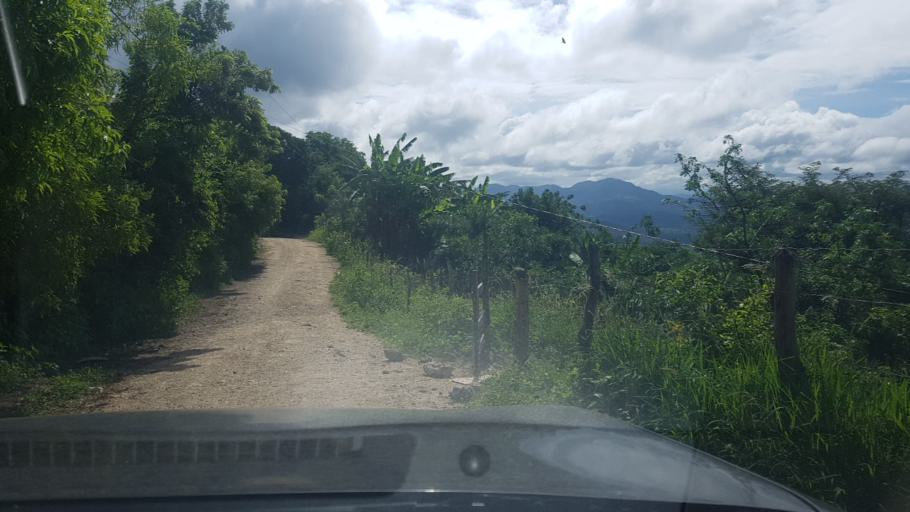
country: NI
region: Madriz
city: Totogalpa
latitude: 13.6043
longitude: -86.6085
